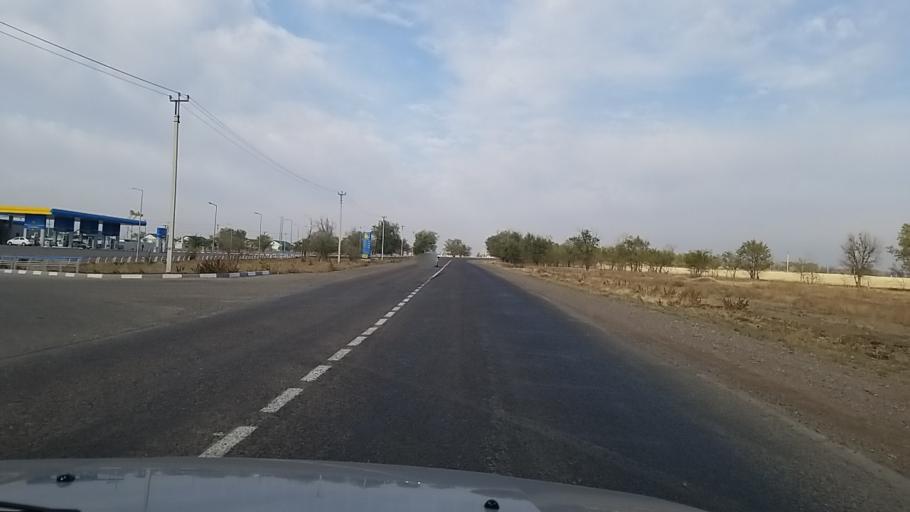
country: KZ
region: Almaty Oblysy
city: Burunday
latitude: 43.4772
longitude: 76.6844
